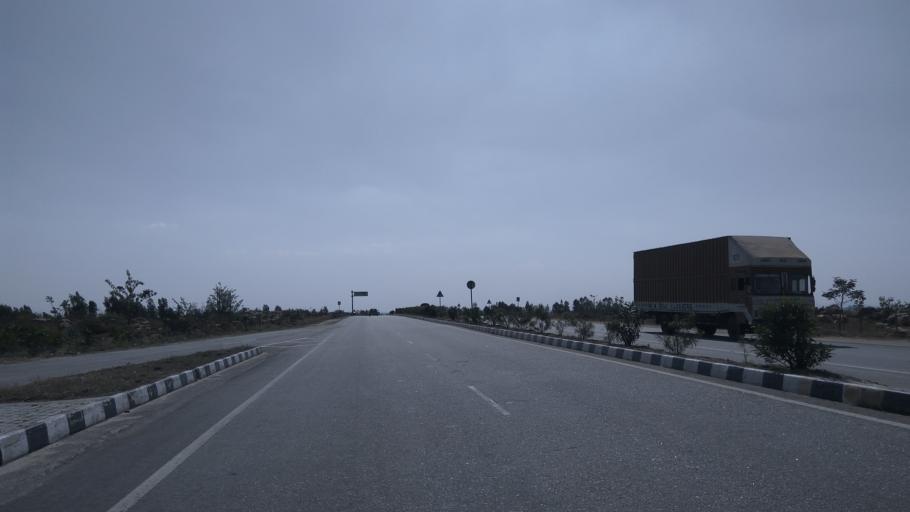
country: IN
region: Karnataka
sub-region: Kolar
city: Mulbagal
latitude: 13.1514
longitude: 78.3019
